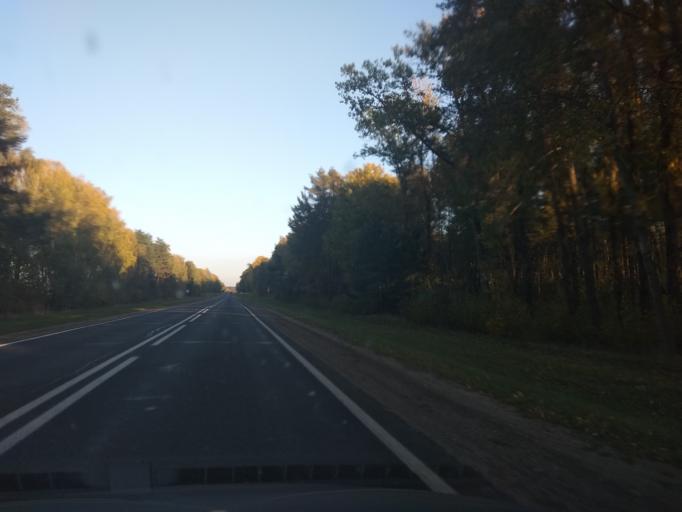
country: BY
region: Grodnenskaya
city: Vawkavysk
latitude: 53.1472
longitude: 24.5903
